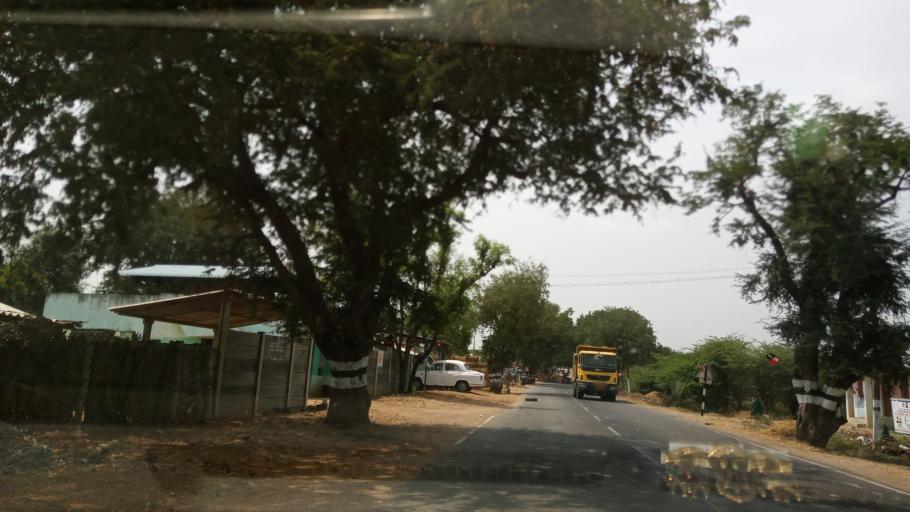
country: IN
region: Tamil Nadu
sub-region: Thanjavur
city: Kumbakonam
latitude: 11.0665
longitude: 79.3608
